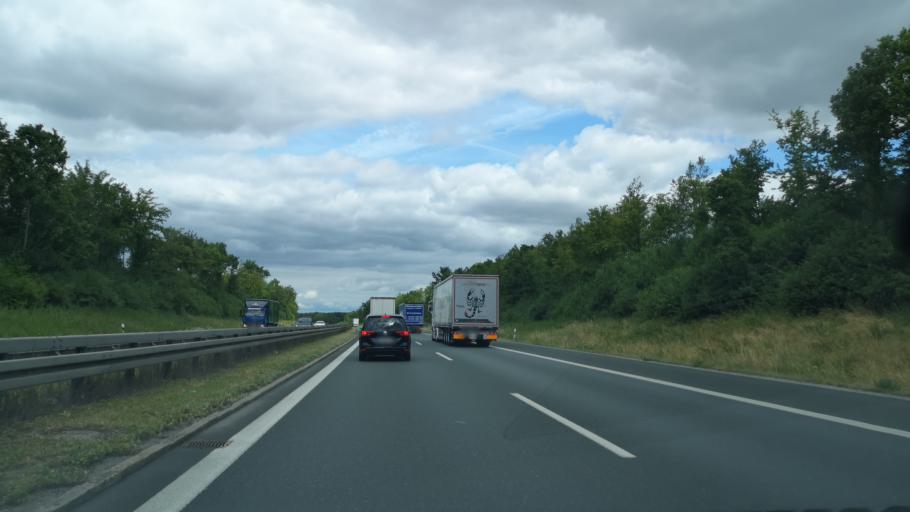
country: DE
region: Bavaria
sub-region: Regierungsbezirk Unterfranken
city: Wasserlosen
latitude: 50.0400
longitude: 10.0671
